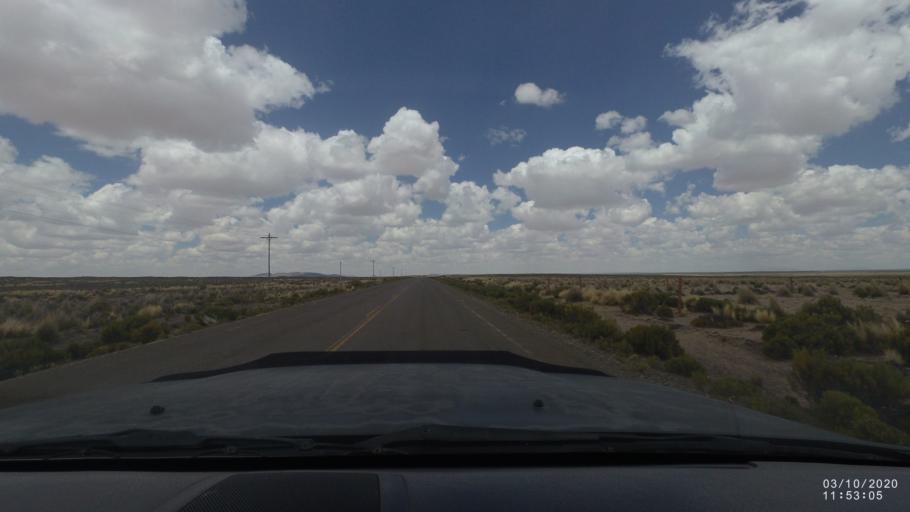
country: BO
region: Oruro
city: Poopo
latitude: -18.4715
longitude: -67.6024
